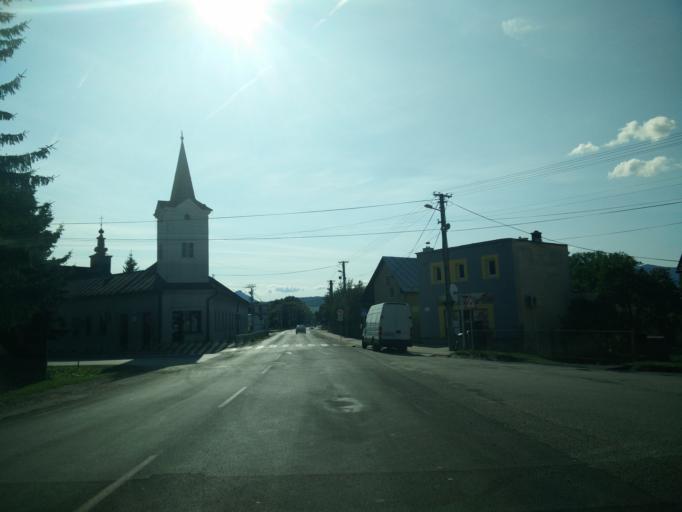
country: SK
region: Zilinsky
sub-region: Okres Martin
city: Martin
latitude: 48.9988
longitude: 18.8827
